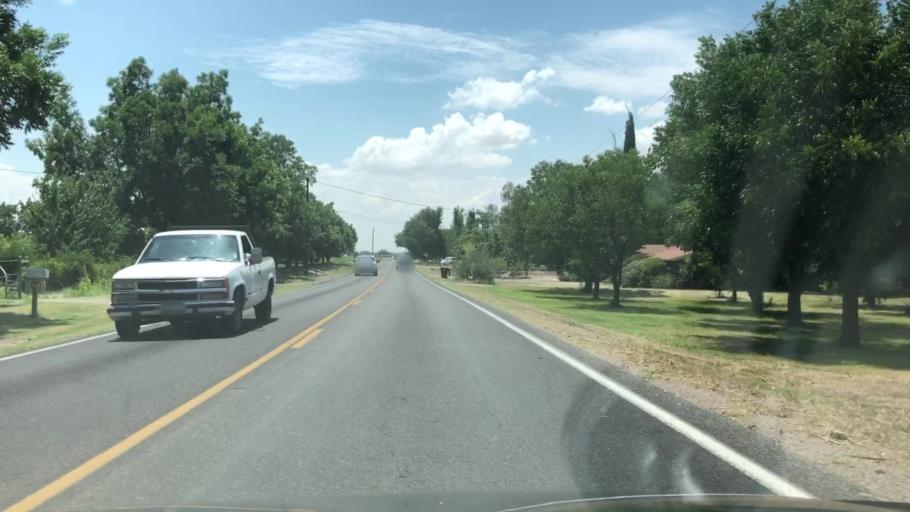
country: US
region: New Mexico
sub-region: Dona Ana County
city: La Union
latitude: 31.9820
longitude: -106.6514
